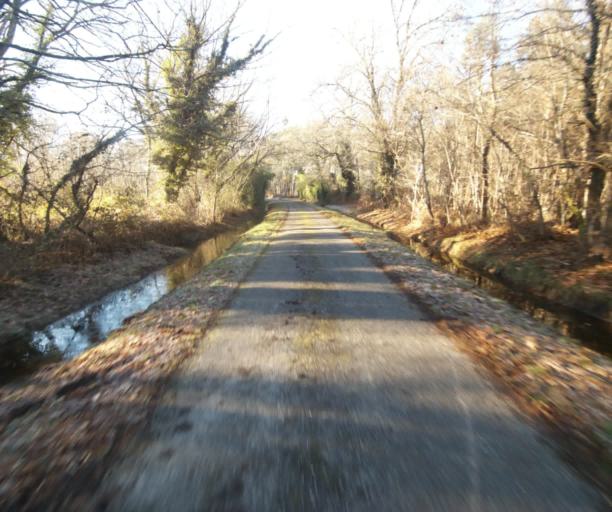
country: FR
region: Aquitaine
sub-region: Departement des Landes
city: Gabarret
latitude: 44.1134
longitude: 0.0606
